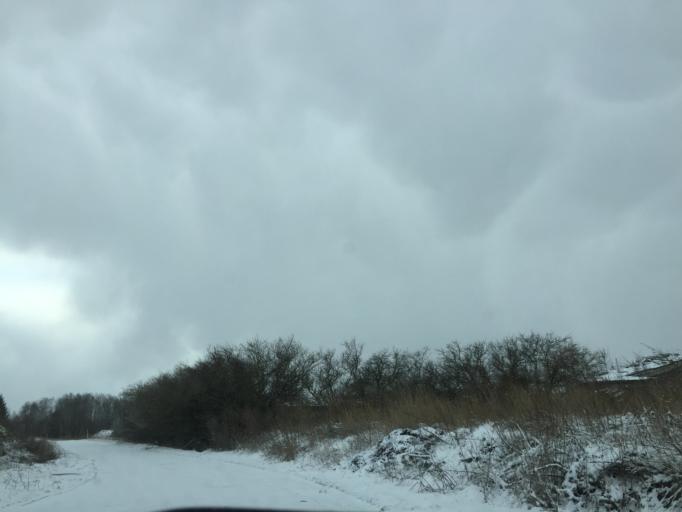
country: LV
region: Ventspils
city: Ventspils
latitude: 57.3710
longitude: 21.6309
